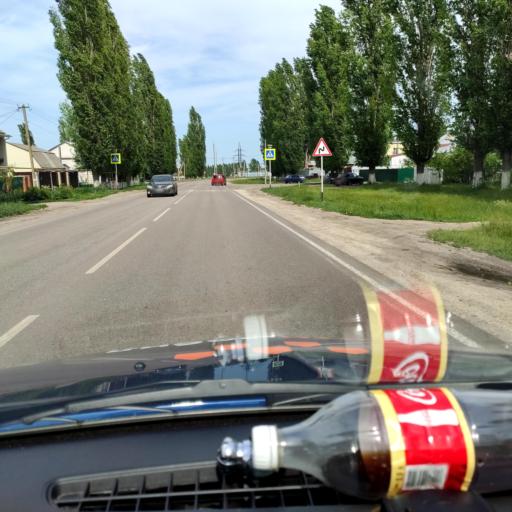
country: RU
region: Voronezj
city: Novaya Usman'
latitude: 51.5438
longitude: 39.3529
